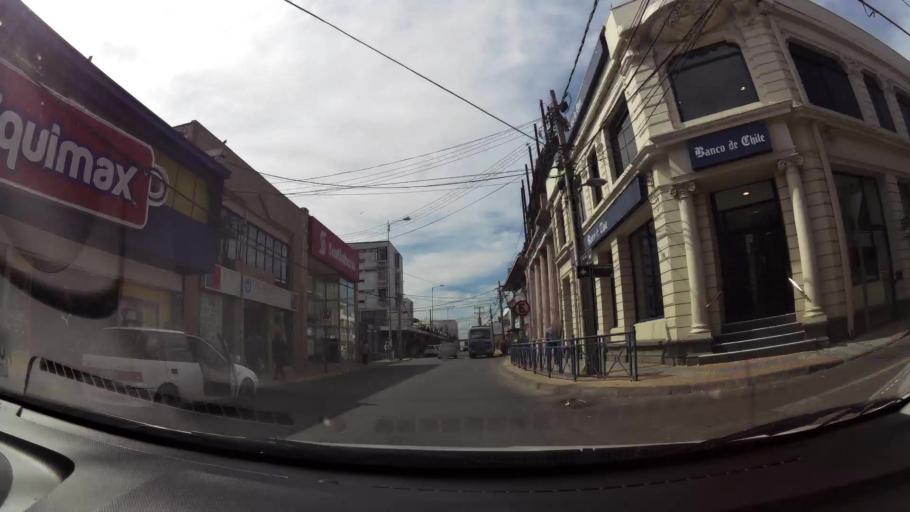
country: CL
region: Biobio
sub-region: Provincia de Concepcion
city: Talcahuano
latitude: -36.7144
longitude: -73.1119
